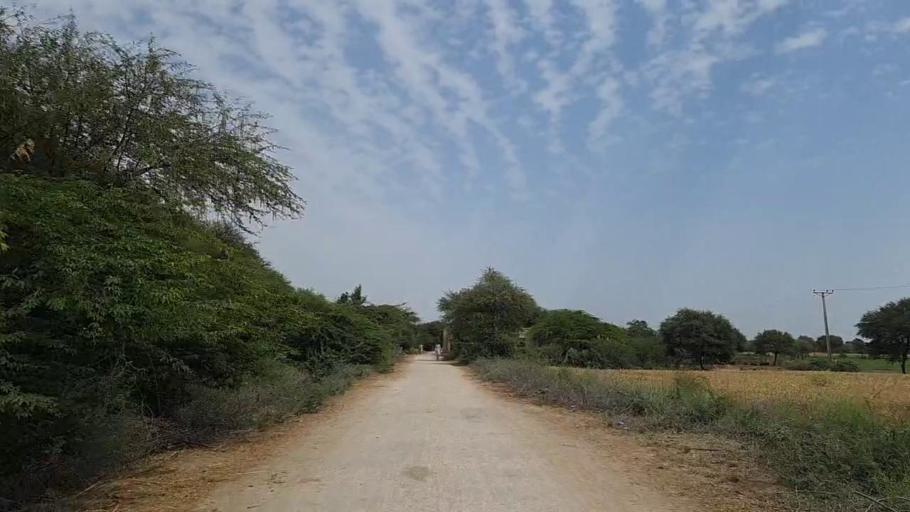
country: PK
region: Sindh
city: Daro Mehar
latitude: 24.7776
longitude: 68.2148
